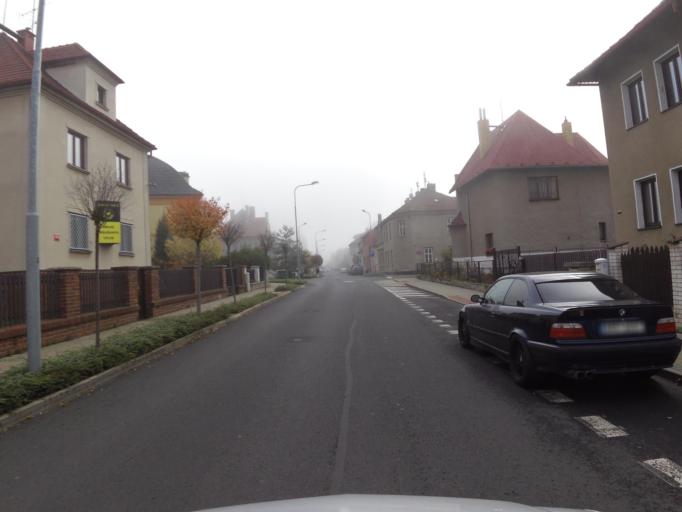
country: CZ
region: Ustecky
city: Zatec
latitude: 50.3230
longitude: 13.5526
